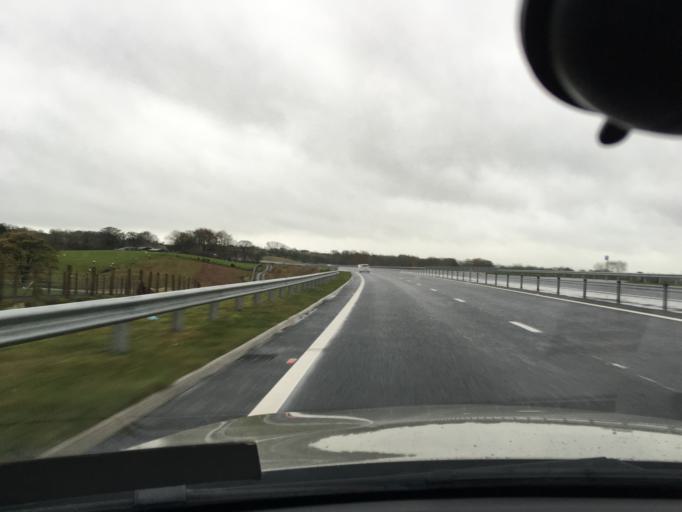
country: GB
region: Northern Ireland
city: Ballyclare
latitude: 54.7751
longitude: -5.9629
